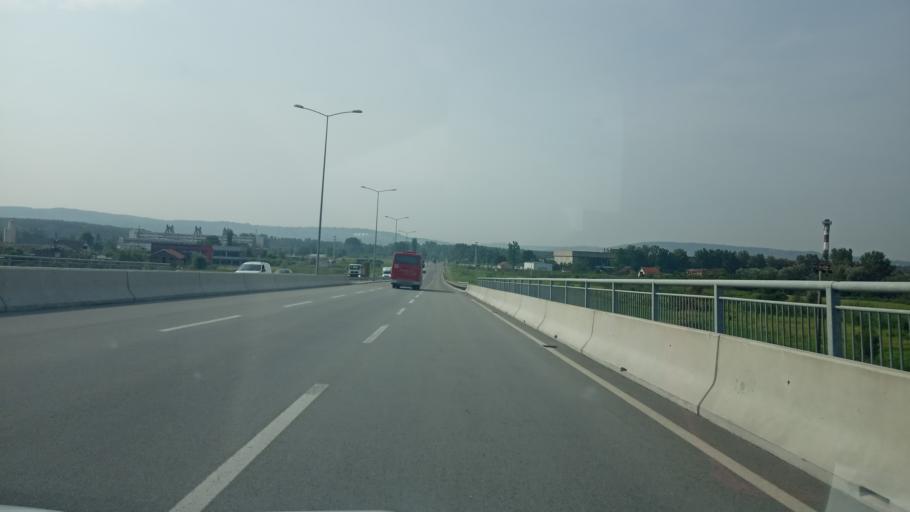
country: RS
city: Ovca
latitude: 44.8554
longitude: 20.5153
